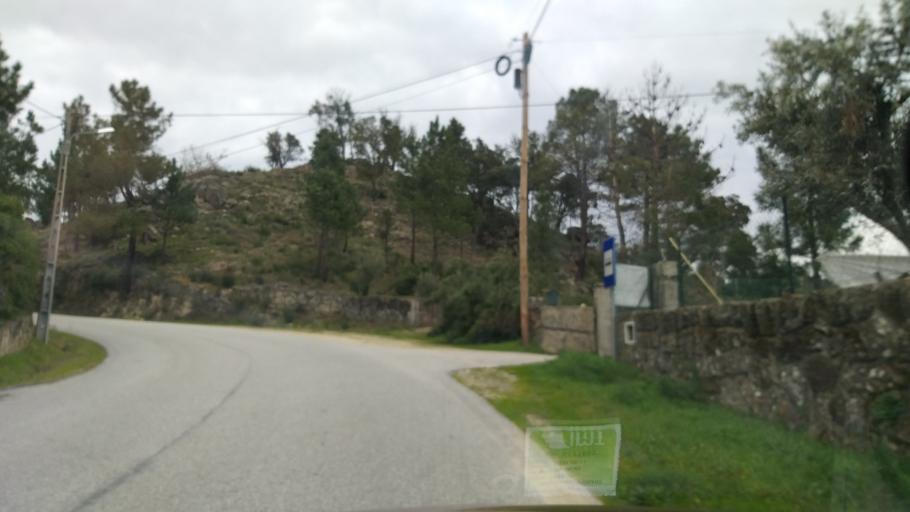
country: PT
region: Guarda
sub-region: Fornos de Algodres
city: Fornos de Algodres
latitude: 40.5736
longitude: -7.6055
